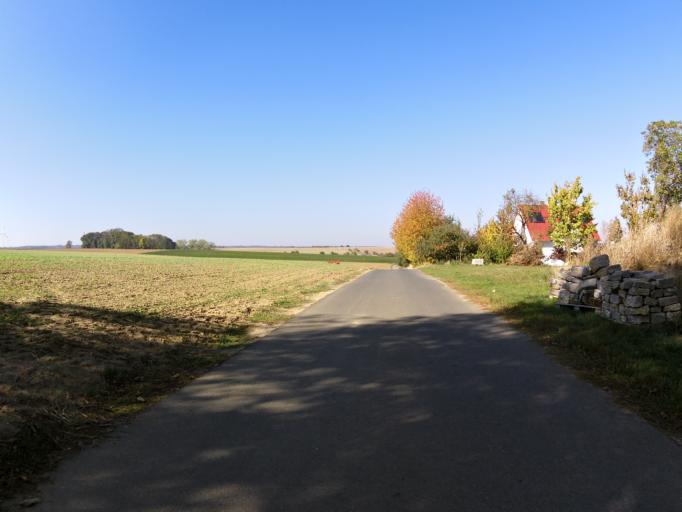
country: DE
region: Bavaria
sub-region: Regierungsbezirk Unterfranken
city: Geroldshausen
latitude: 49.6924
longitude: 9.9264
